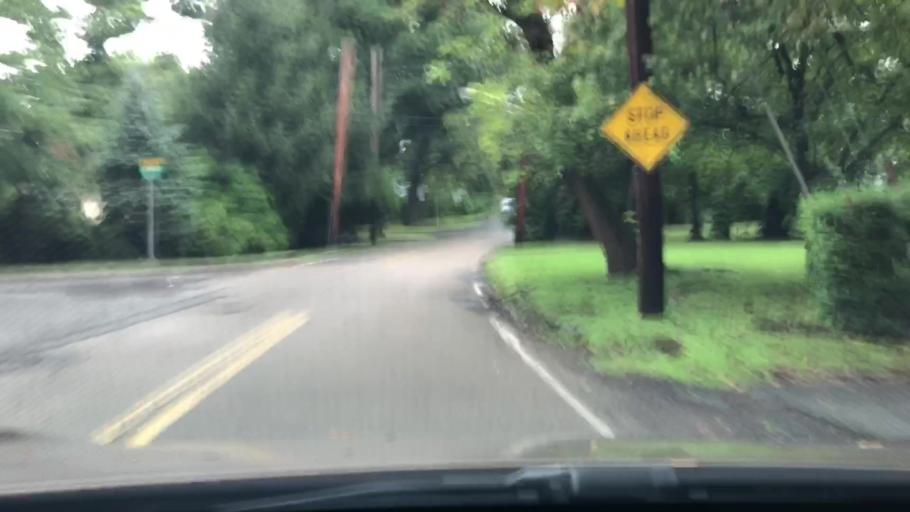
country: US
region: New York
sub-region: Westchester County
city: Scarsdale
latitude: 41.0081
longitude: -73.7726
